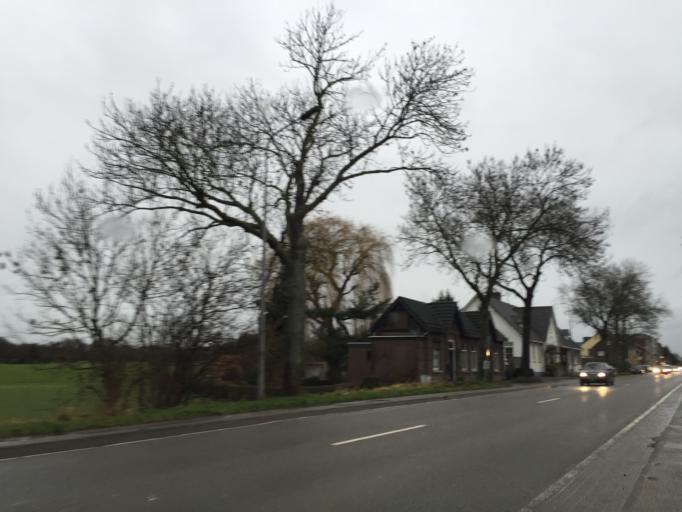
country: BE
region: Flanders
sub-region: Provincie Limburg
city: Lanaken
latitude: 50.8799
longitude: 5.6731
